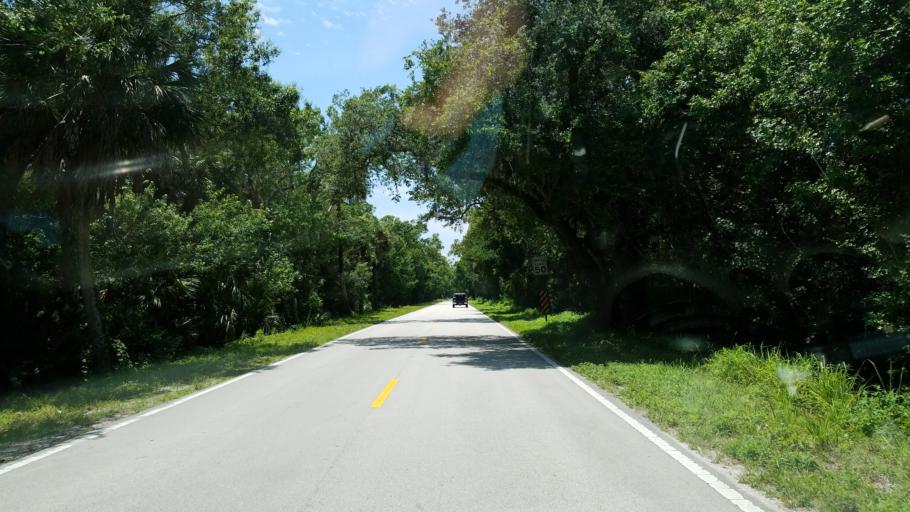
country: US
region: Florida
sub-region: Martin County
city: Indiantown
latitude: 27.1621
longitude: -80.5628
